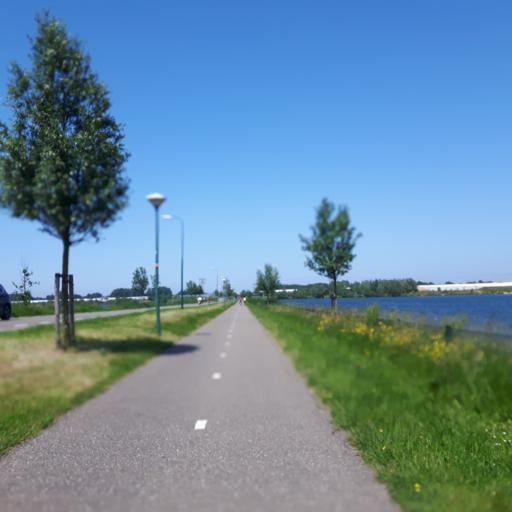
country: NL
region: Utrecht
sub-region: Stichtse Vecht
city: Spechtenkamp
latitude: 52.1166
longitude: 5.0169
